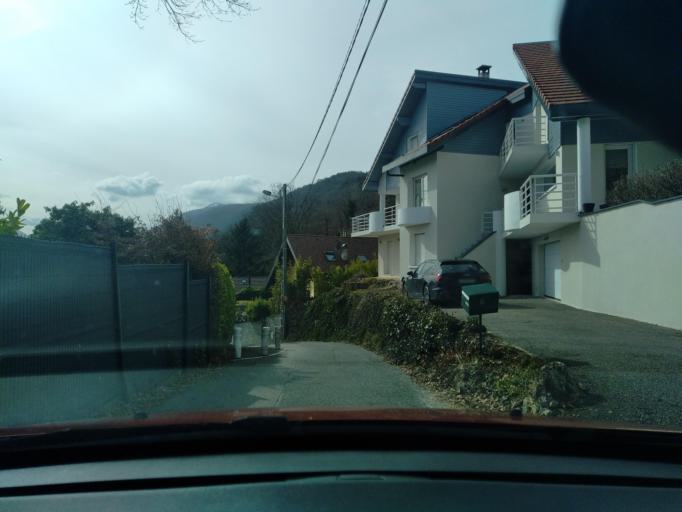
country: FR
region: Rhone-Alpes
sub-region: Departement de la Haute-Savoie
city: Sevrier
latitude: 45.8854
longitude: 6.1408
